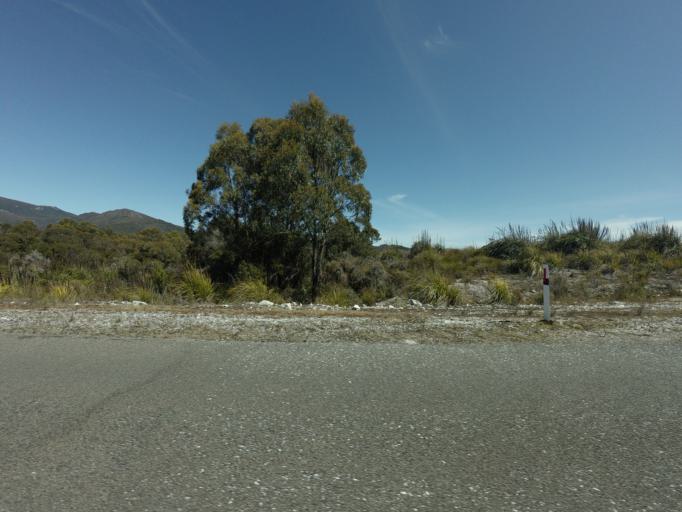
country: AU
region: Tasmania
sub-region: Huon Valley
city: Geeveston
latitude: -42.8397
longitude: 146.1593
